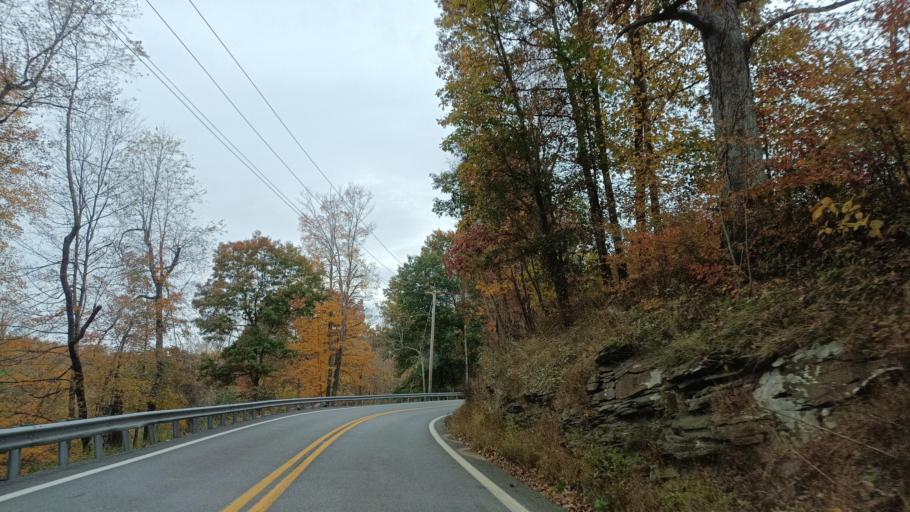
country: US
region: West Virginia
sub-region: Taylor County
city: Grafton
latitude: 39.3300
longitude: -79.9162
